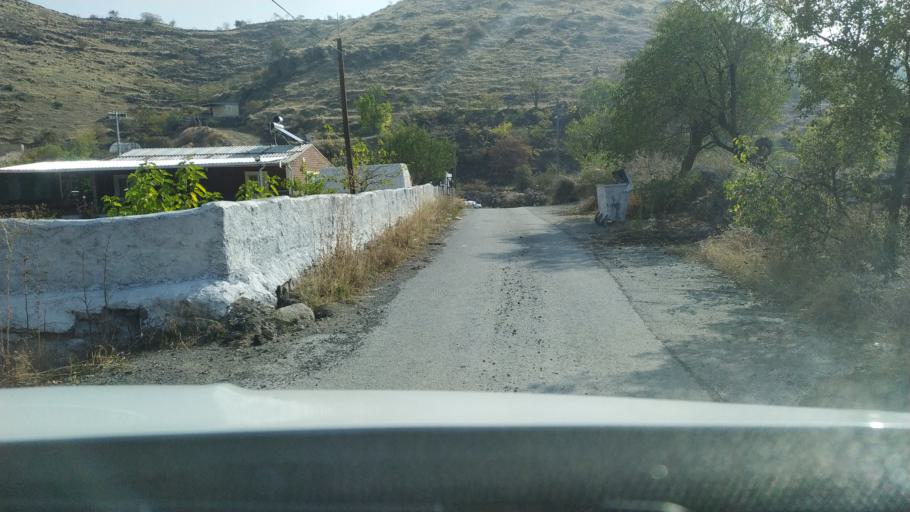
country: TR
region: Kayseri
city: Hacilar
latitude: 38.6801
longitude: 35.4424
